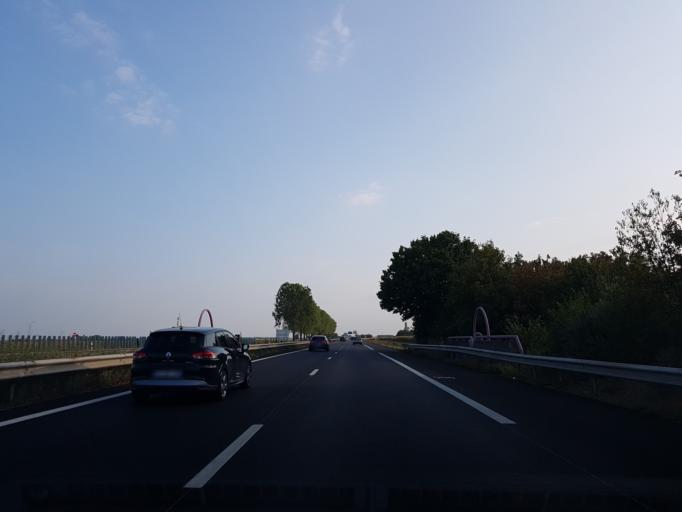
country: FR
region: Alsace
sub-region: Departement du Haut-Rhin
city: Oberhergheim
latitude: 47.9616
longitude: 7.3688
